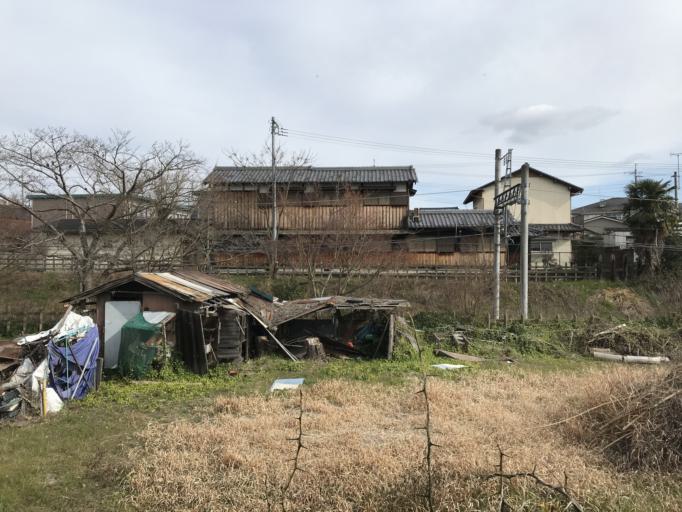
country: JP
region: Mie
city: Ueno-ebisumachi
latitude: 34.7582
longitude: 136.1351
